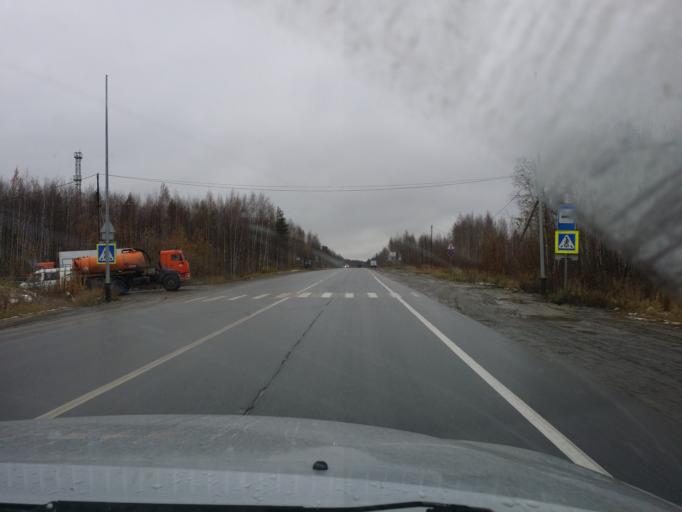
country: RU
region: Khanty-Mansiyskiy Avtonomnyy Okrug
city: Megion
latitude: 61.0897
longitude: 76.0960
